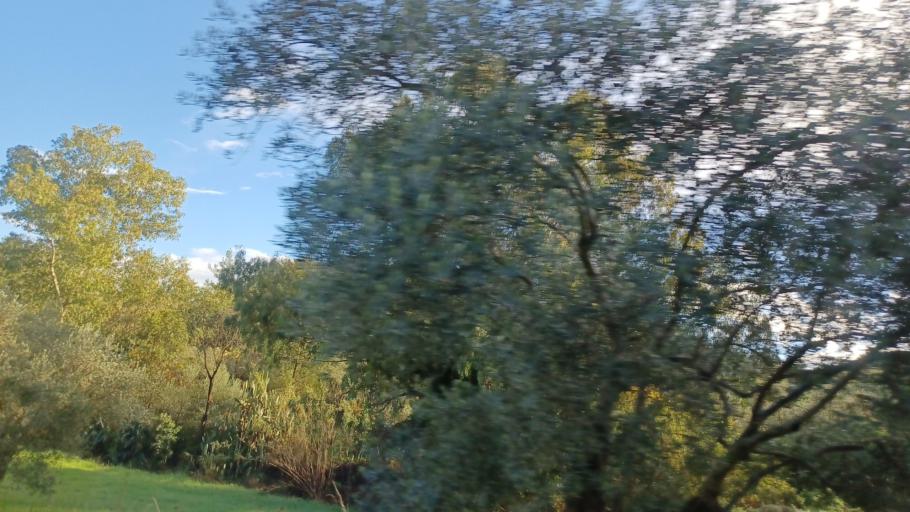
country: CY
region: Lefkosia
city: Lythrodontas
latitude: 34.9342
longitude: 33.2977
